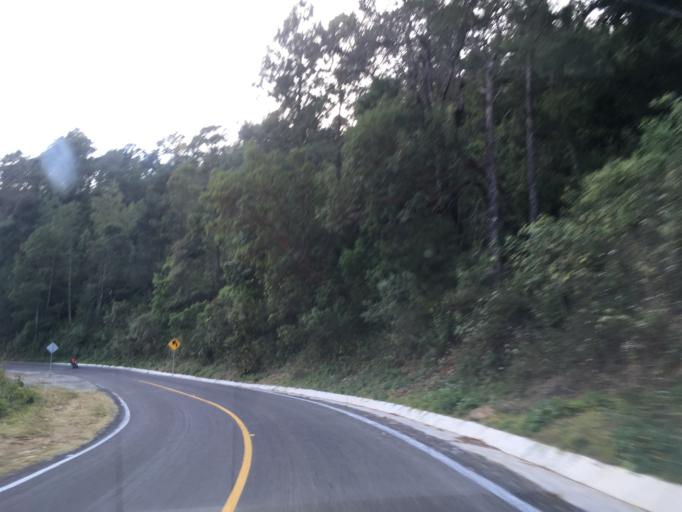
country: MX
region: Michoacan
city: Tzitzio
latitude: 19.6718
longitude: -100.9078
